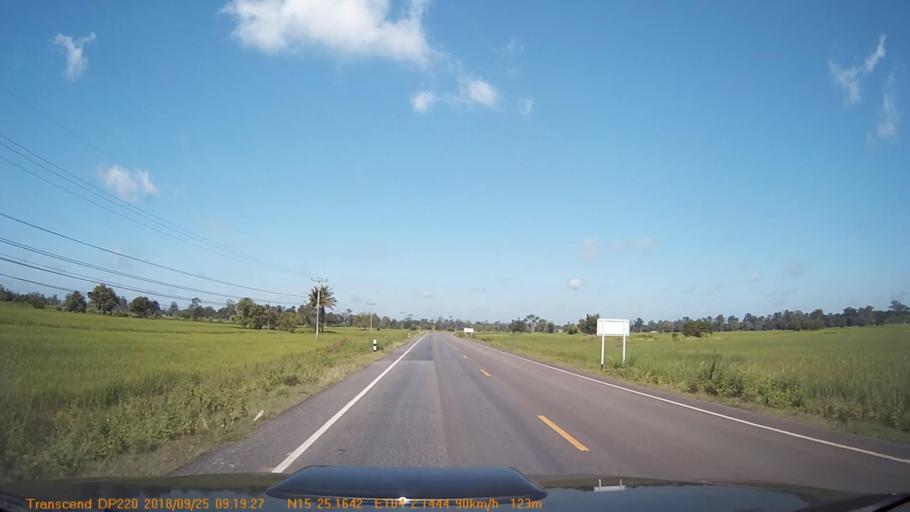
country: TH
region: Sisaket
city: Sila Lat
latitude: 15.4193
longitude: 104.0361
